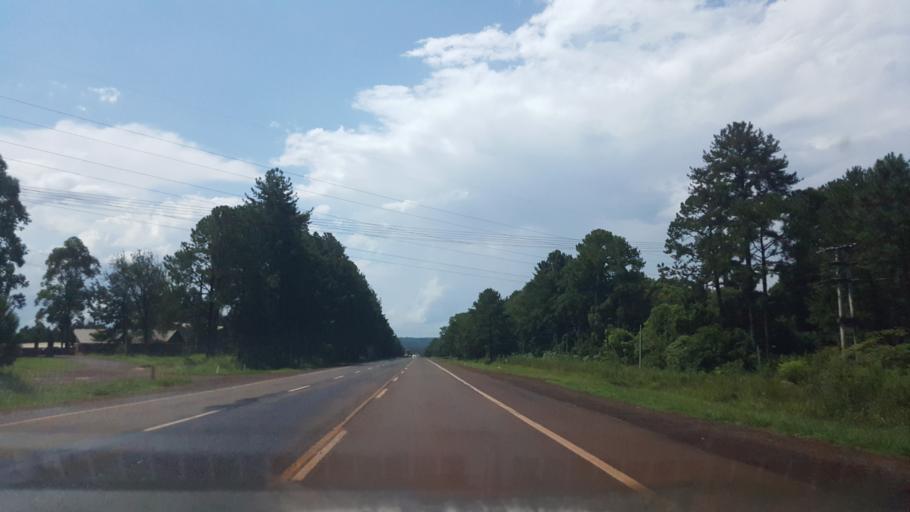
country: AR
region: Misiones
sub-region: Departamento de Eldorado
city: Eldorado
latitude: -26.3817
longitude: -54.6276
